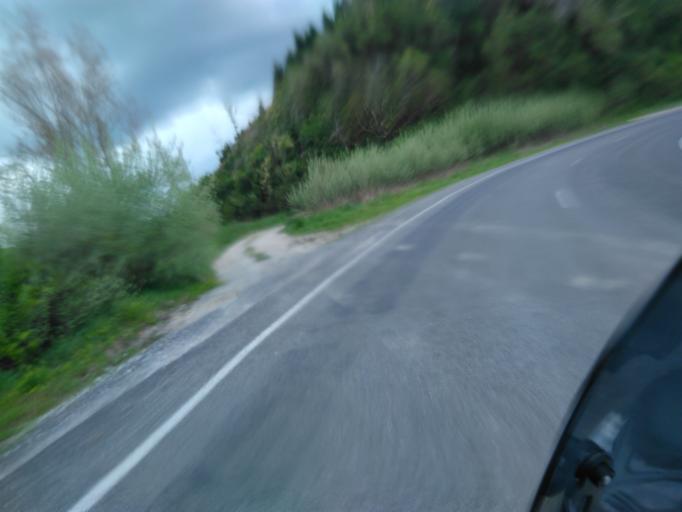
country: NZ
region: Gisborne
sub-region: Gisborne District
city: Gisborne
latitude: -38.6734
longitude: 177.8108
